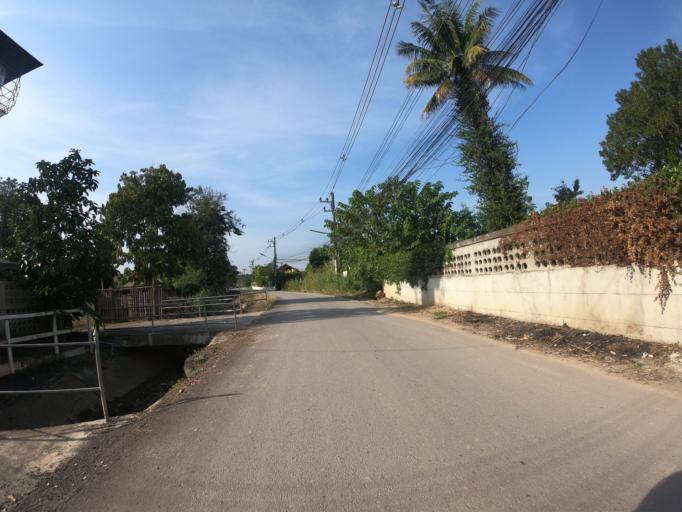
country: TH
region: Chiang Mai
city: Chiang Mai
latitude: 18.8335
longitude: 98.9959
